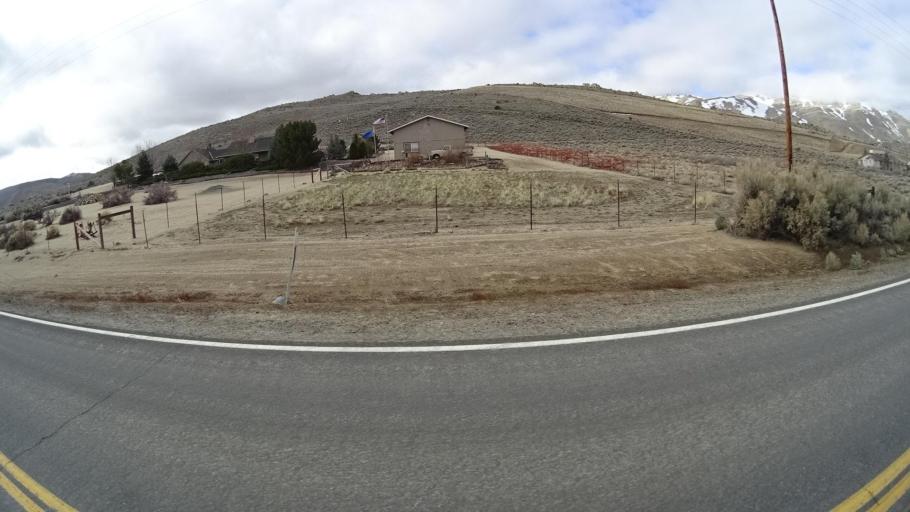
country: US
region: Nevada
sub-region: Washoe County
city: Cold Springs
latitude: 39.8619
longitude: -119.9386
